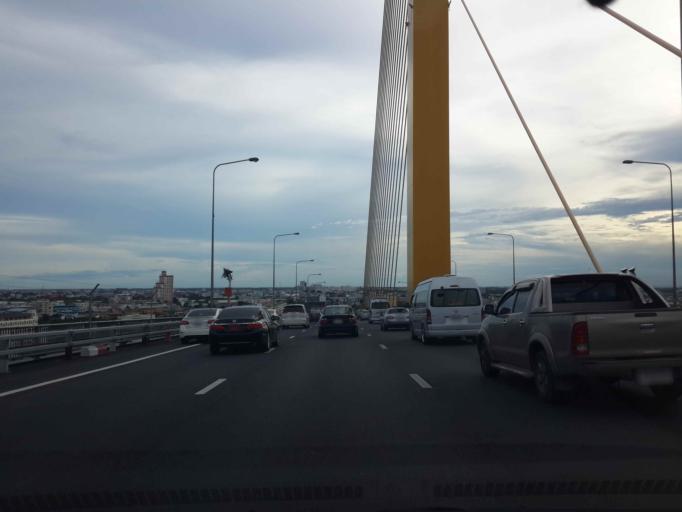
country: TH
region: Bangkok
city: Rat Burana
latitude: 13.6810
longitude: 100.5168
